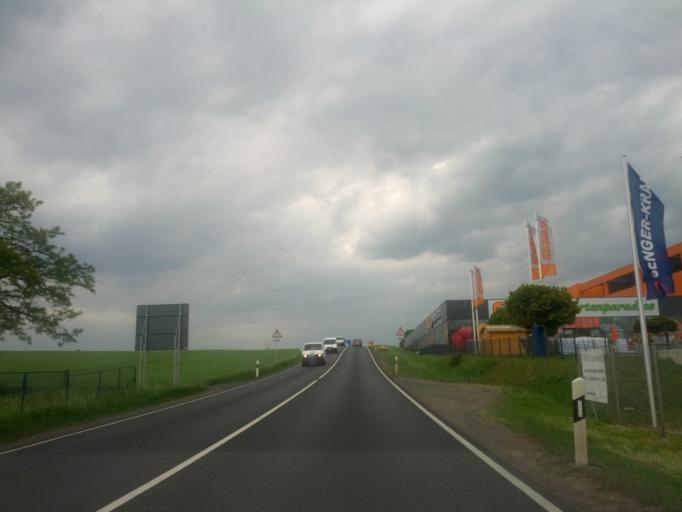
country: DE
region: Thuringia
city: Schwabhausen
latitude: 50.8926
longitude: 10.7279
